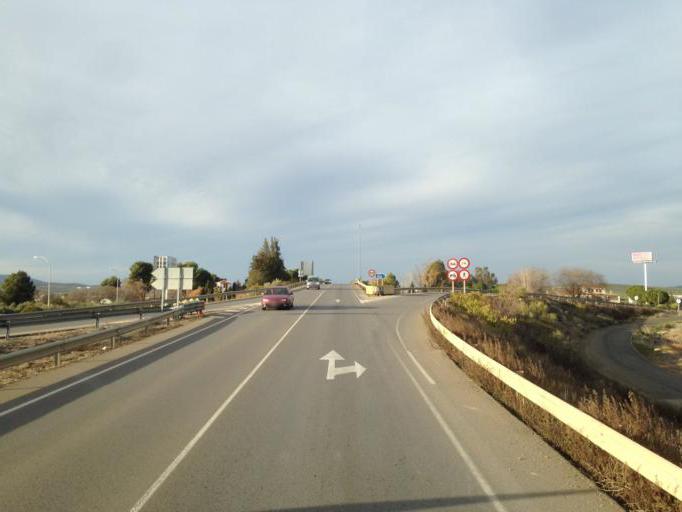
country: ES
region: Andalusia
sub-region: Provincia de Malaga
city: Antequera
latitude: 37.0701
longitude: -4.5652
